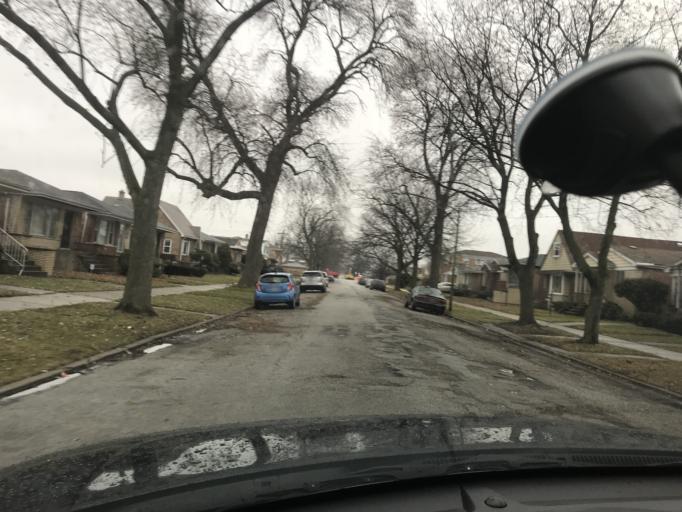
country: US
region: Illinois
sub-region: Cook County
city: Calumet Park
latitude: 41.7198
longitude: -87.6383
